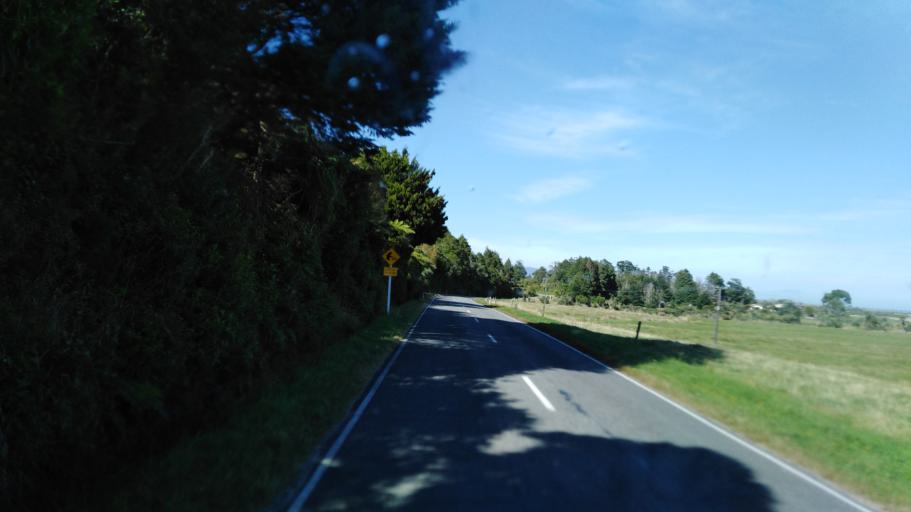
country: NZ
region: West Coast
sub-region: Buller District
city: Westport
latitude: -41.2669
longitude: 172.1115
